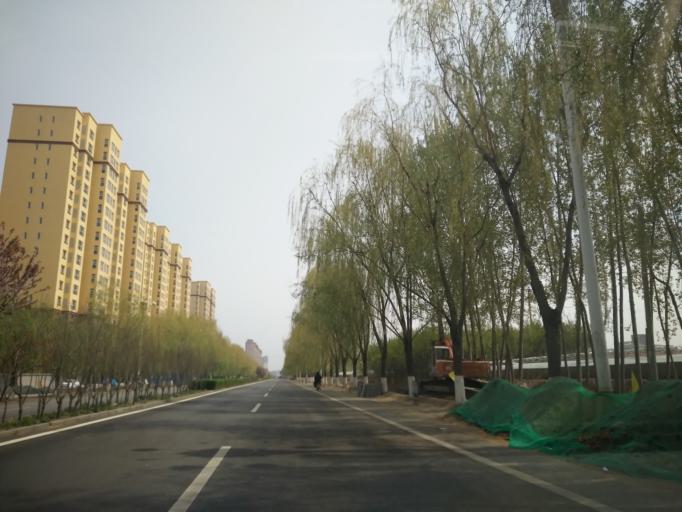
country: CN
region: Beijing
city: Xiji
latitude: 39.7450
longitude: 116.9733
